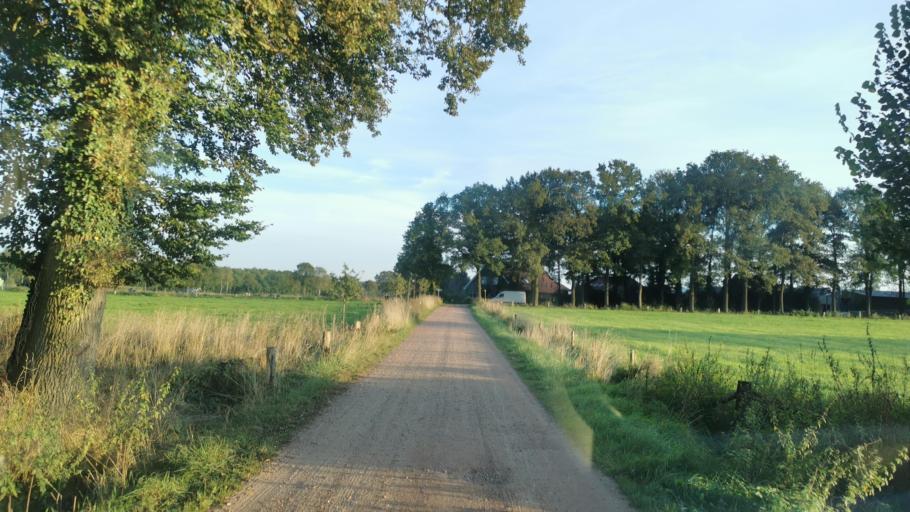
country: NL
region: Overijssel
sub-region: Gemeente Losser
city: Losser
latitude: 52.3025
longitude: 6.9823
